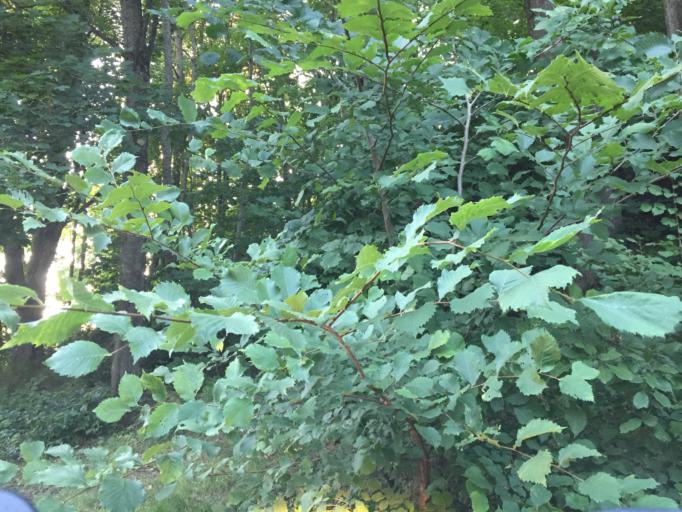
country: LV
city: Tervete
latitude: 56.4806
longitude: 23.3876
